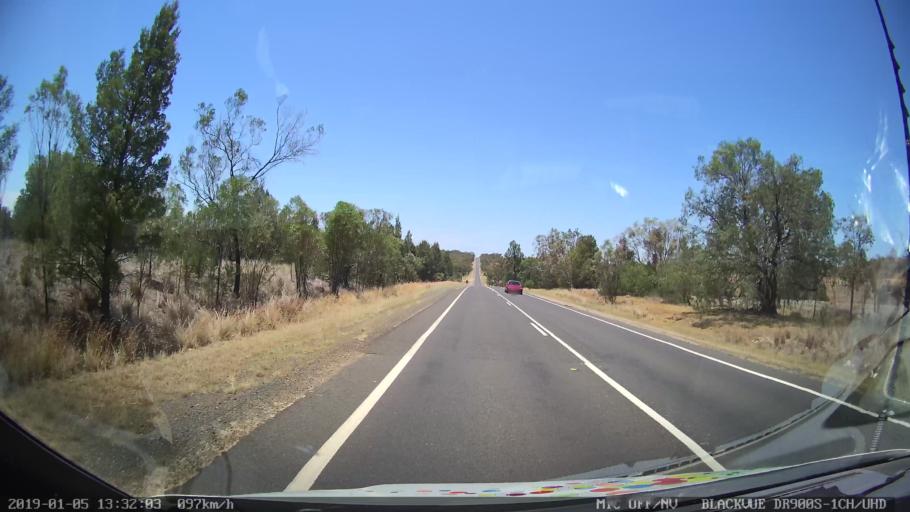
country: AU
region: New South Wales
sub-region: Gunnedah
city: Gunnedah
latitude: -31.0078
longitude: 150.0936
